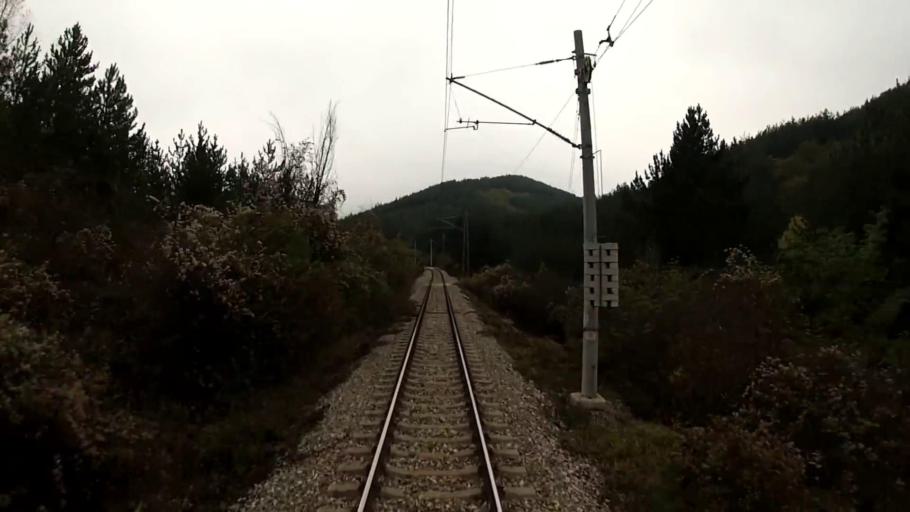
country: BG
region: Sofiya
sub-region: Obshtina Dragoman
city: Dragoman
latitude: 42.9478
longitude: 22.9017
